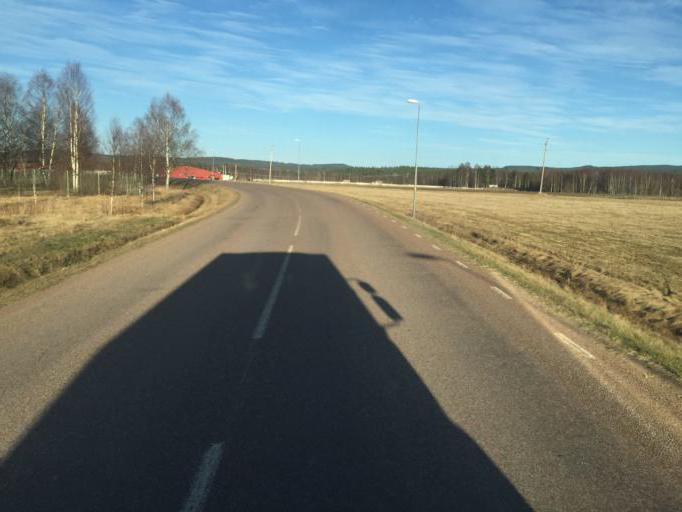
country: SE
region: Dalarna
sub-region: Gagnefs Kommun
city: Mockfjard
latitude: 60.4938
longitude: 14.9623
